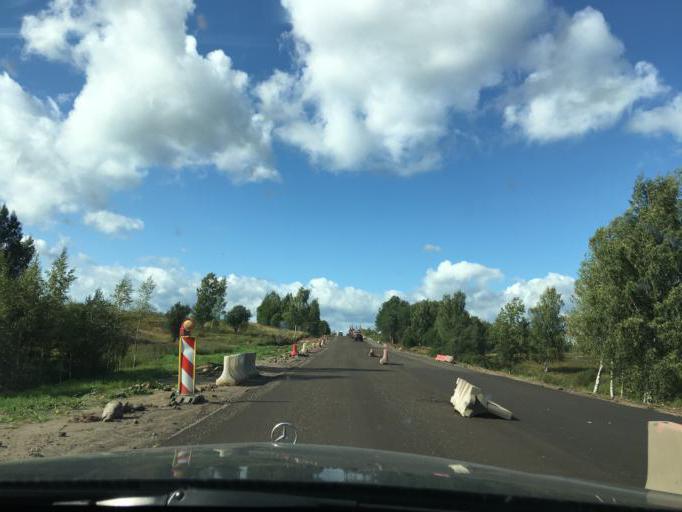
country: RU
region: Pskov
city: Velikiye Luki
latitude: 56.2704
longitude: 30.3745
